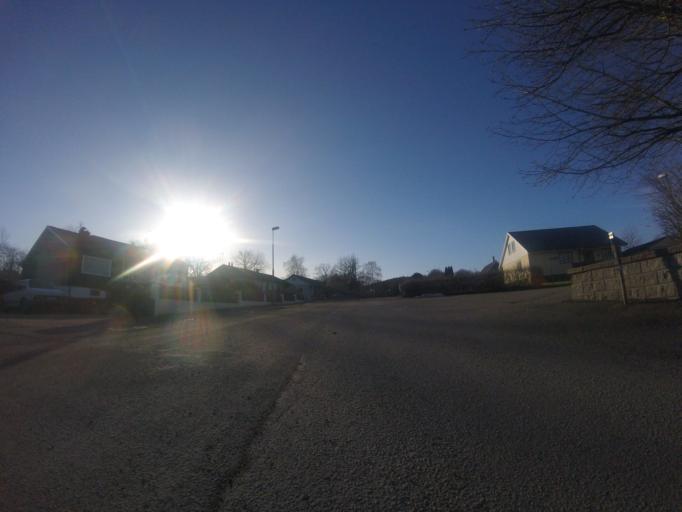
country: SE
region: Halland
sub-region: Varbergs Kommun
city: Veddige
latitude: 57.2329
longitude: 12.3121
